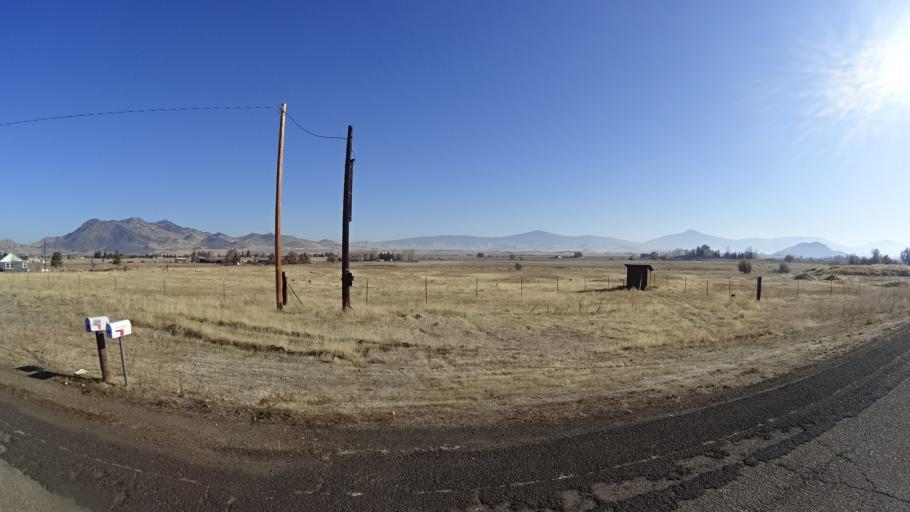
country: US
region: California
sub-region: Siskiyou County
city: Yreka
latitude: 41.7363
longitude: -122.5931
